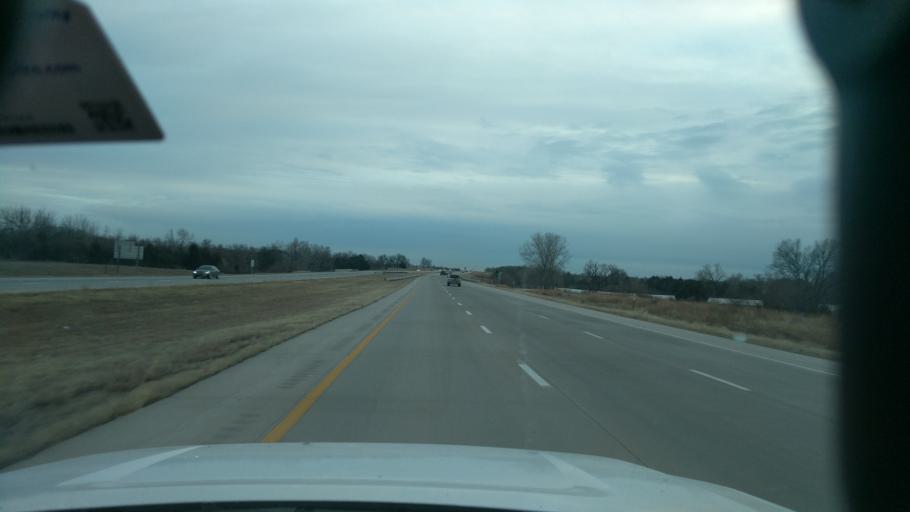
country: US
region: Kansas
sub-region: Sedgwick County
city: Valley Center
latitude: 37.9094
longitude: -97.3266
